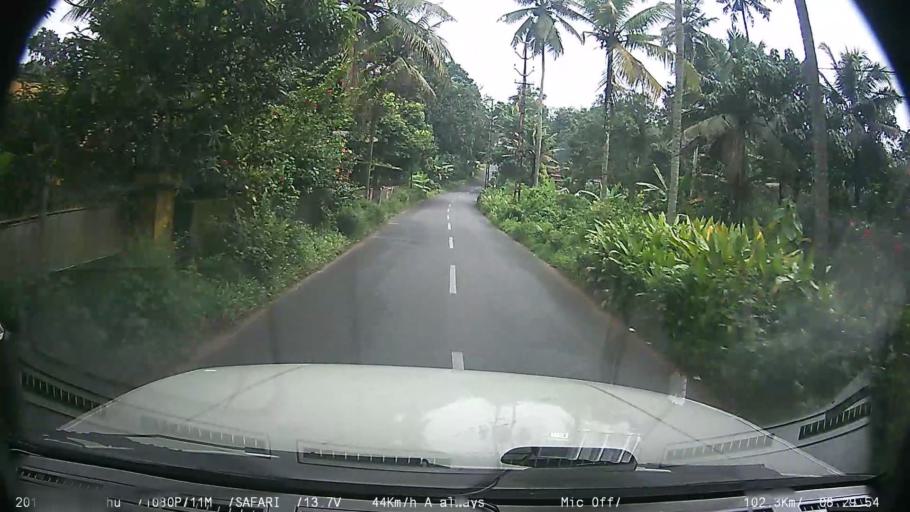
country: IN
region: Kerala
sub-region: Kottayam
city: Palackattumala
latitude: 9.6891
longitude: 76.6097
